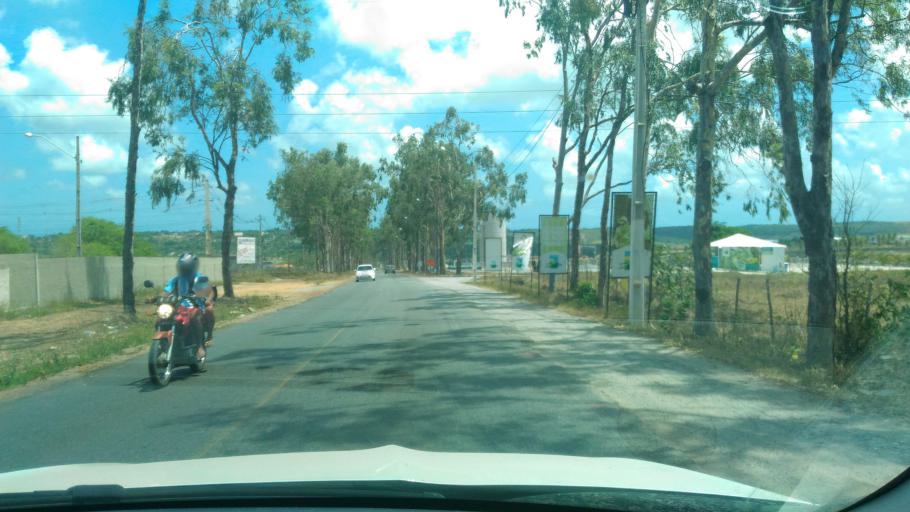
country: BR
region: Paraiba
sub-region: Conde
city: Conde
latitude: -7.2604
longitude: -34.9342
